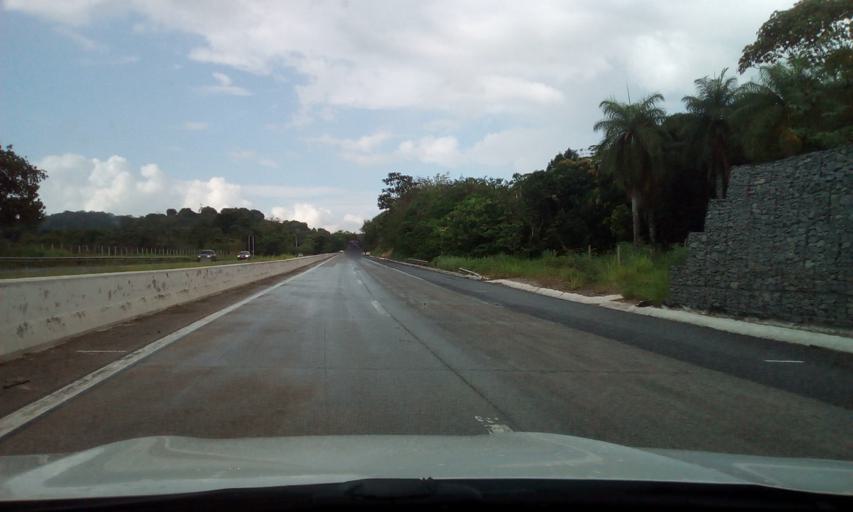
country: BR
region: Pernambuco
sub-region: Cabo De Santo Agostinho
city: Cabo
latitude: -8.3151
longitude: -35.1039
